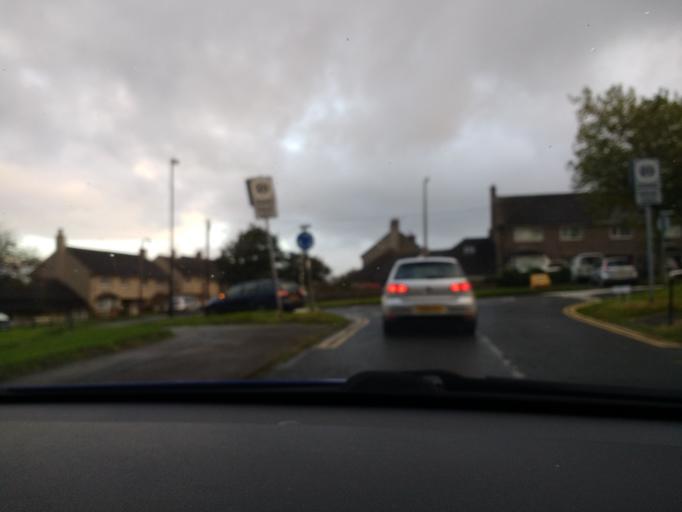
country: GB
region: England
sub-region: Lancashire
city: Lancaster
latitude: 54.0527
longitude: -2.7899
